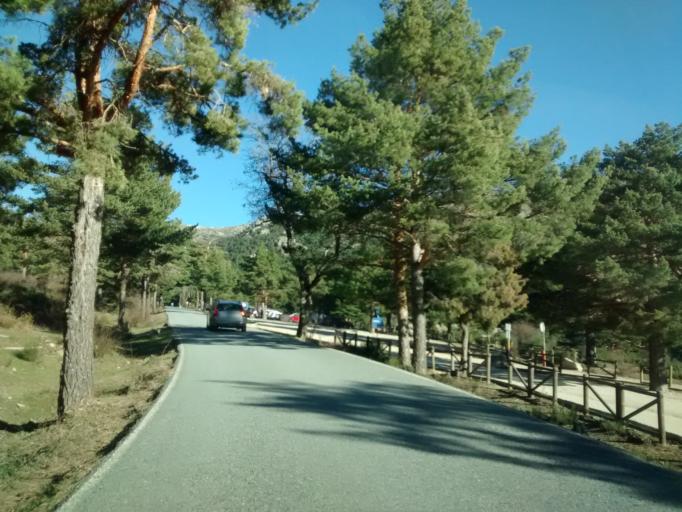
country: ES
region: Madrid
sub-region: Provincia de Madrid
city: Navacerrada
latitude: 40.7504
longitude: -3.9933
